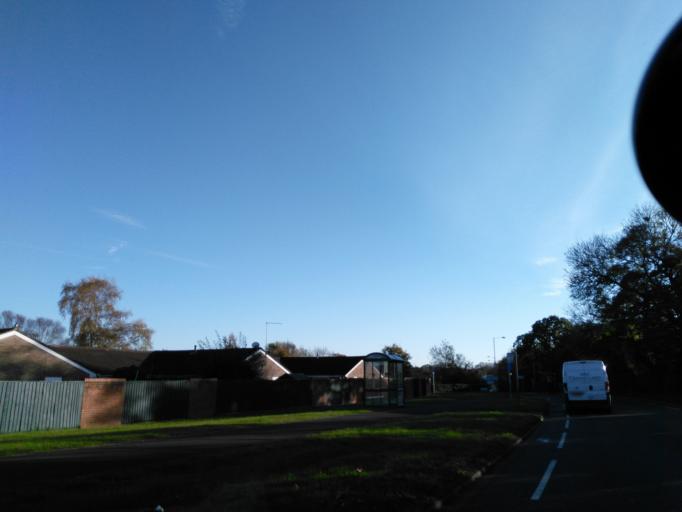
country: GB
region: England
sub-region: Wiltshire
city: Chippenham
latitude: 51.4517
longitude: -2.1394
